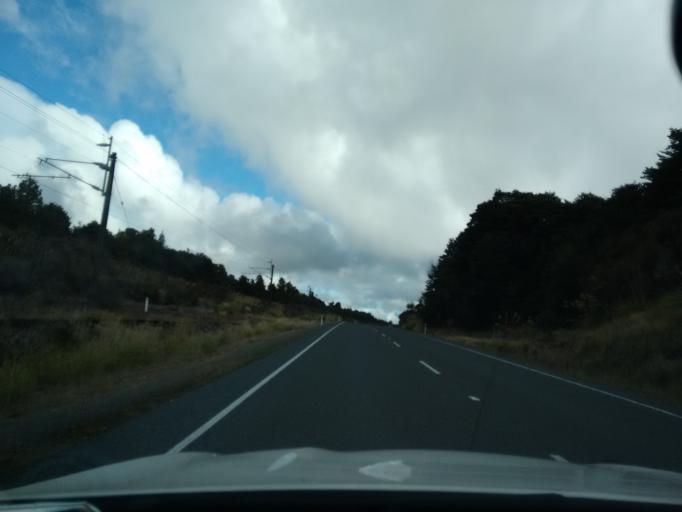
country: NZ
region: Manawatu-Wanganui
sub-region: Ruapehu District
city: Waiouru
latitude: -39.3063
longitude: 175.3898
